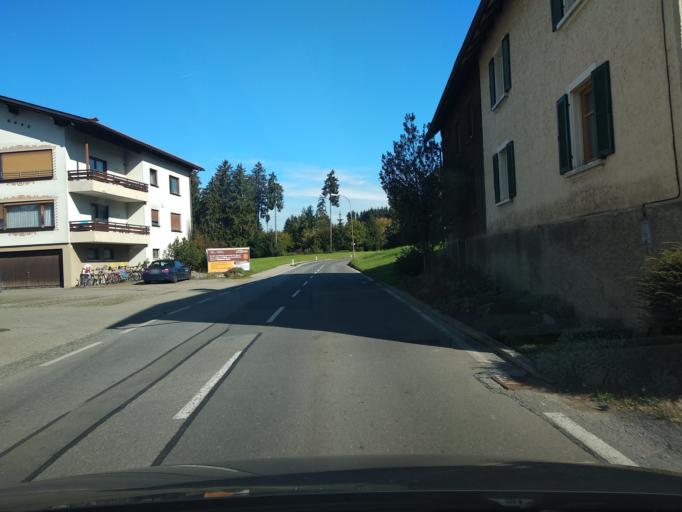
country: DE
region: Bavaria
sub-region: Swabia
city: Sigmarszell
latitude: 47.5746
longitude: 9.7725
